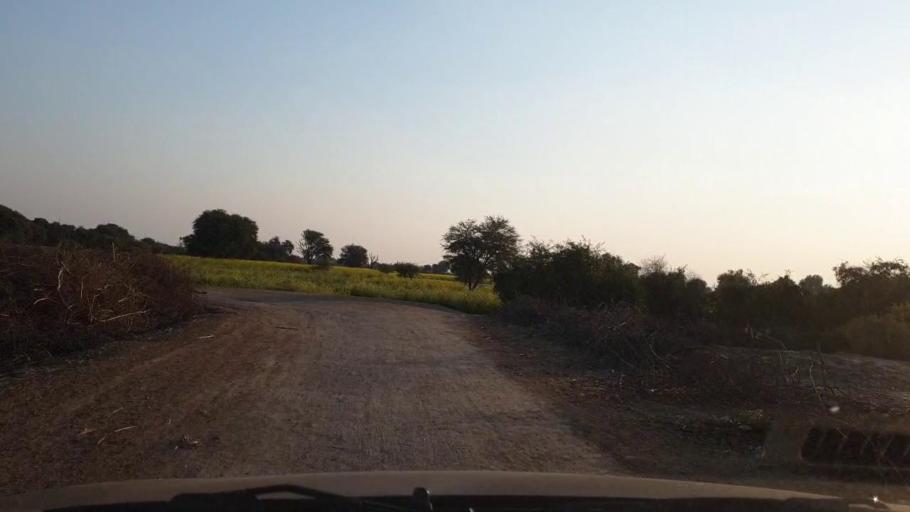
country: PK
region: Sindh
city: Jhol
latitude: 25.9164
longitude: 68.9335
